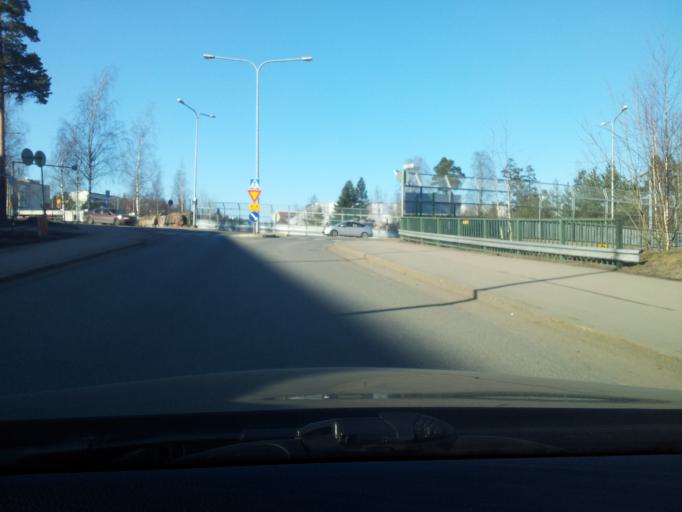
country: FI
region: Uusimaa
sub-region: Helsinki
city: Vantaa
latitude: 60.2226
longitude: 25.0771
